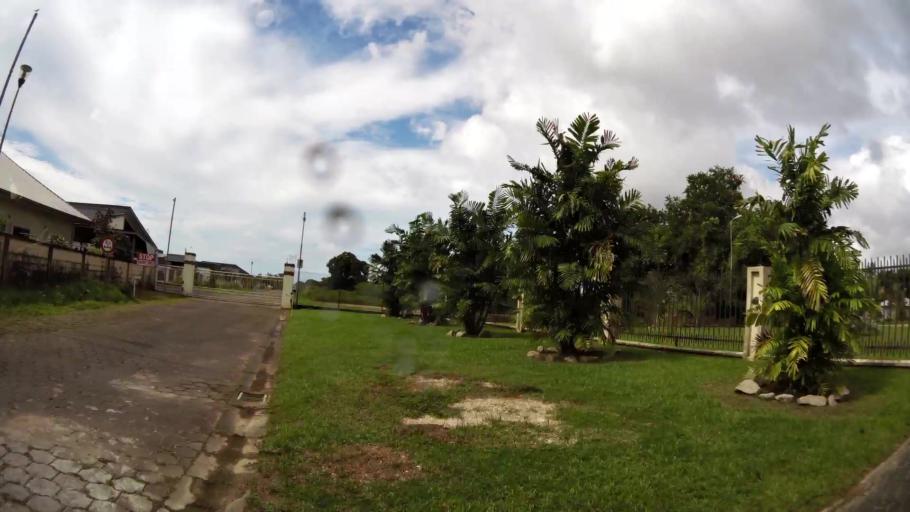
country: SR
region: Paramaribo
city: Paramaribo
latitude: 5.8470
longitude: -55.1904
